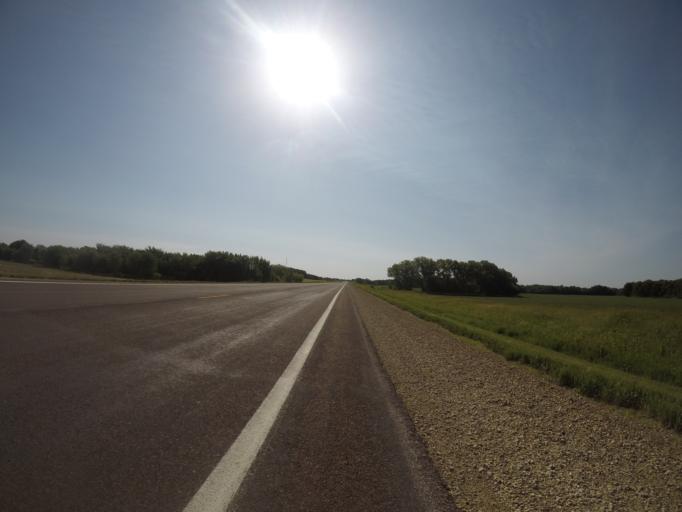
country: US
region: Kansas
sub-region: Riley County
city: Fort Riley North
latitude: 39.3057
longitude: -96.8482
